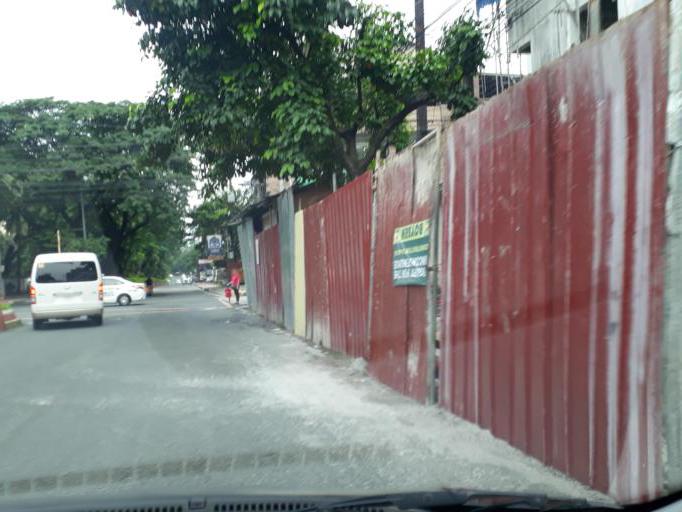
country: PH
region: Calabarzon
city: Del Monte
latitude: 14.6304
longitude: 121.0259
